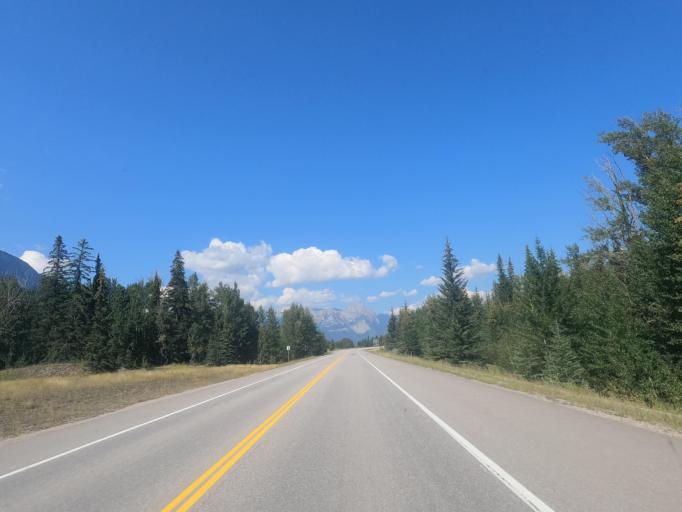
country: CA
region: Alberta
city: Jasper Park Lodge
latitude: 52.9671
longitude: -118.0546
